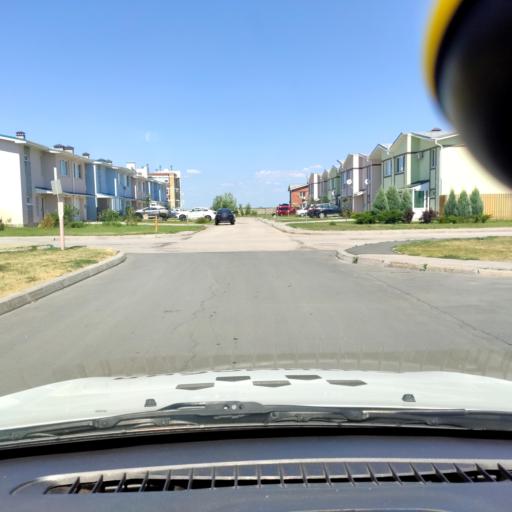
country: RU
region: Samara
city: Tol'yatti
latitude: 53.6184
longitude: 49.3172
